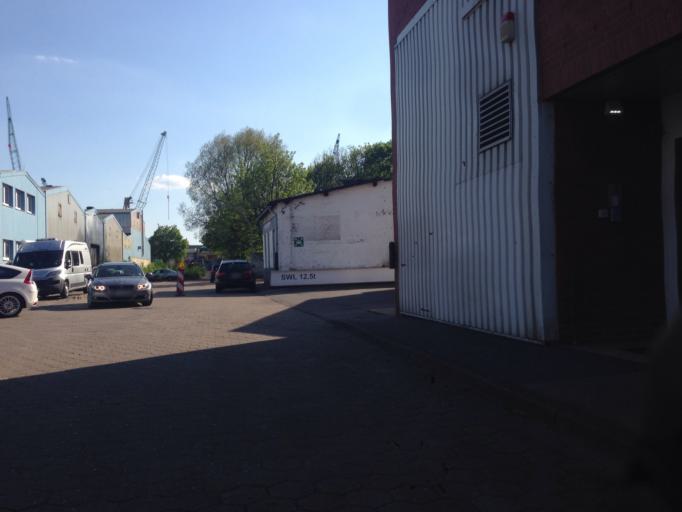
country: DE
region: Hamburg
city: Neustadt
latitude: 53.5382
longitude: 9.9761
